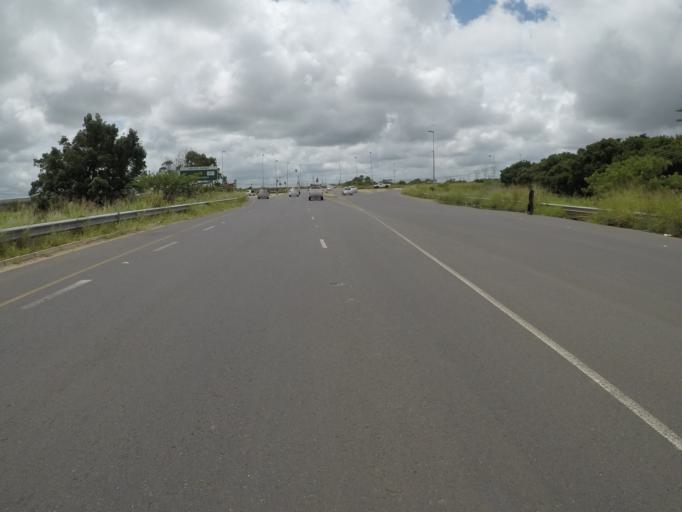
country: ZA
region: KwaZulu-Natal
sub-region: uThungulu District Municipality
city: Empangeni
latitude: -28.7765
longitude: 31.9582
